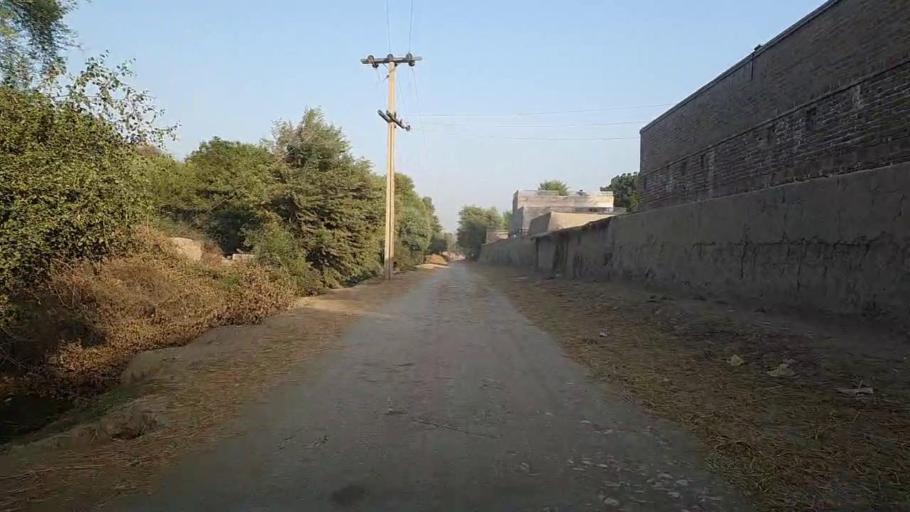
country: PK
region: Sindh
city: Kashmor
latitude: 28.4285
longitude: 69.4633
